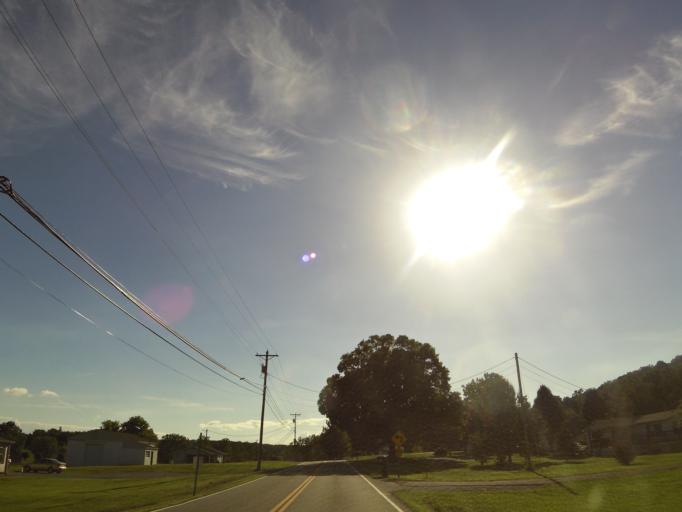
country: US
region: Tennessee
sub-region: Greene County
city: Greeneville
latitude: 36.1332
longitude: -82.8866
